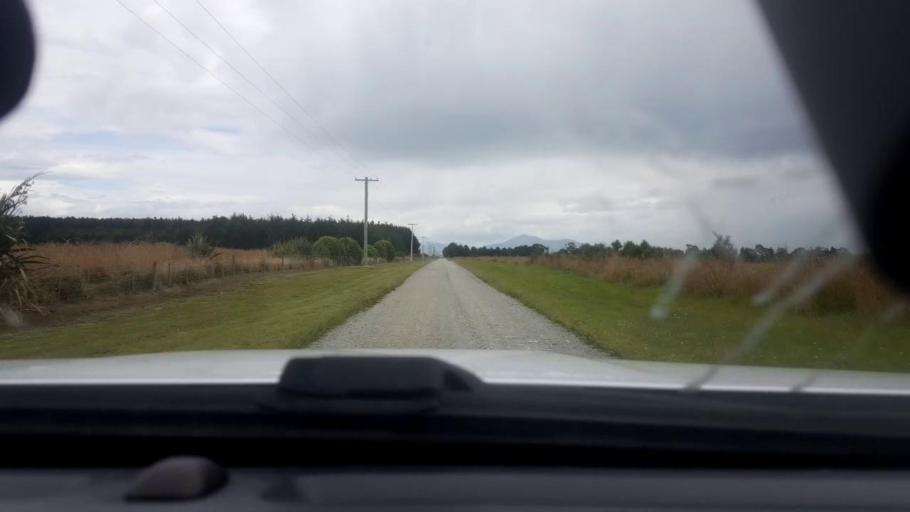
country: NZ
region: Canterbury
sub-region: Timaru District
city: Timaru
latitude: -44.1634
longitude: 171.4071
